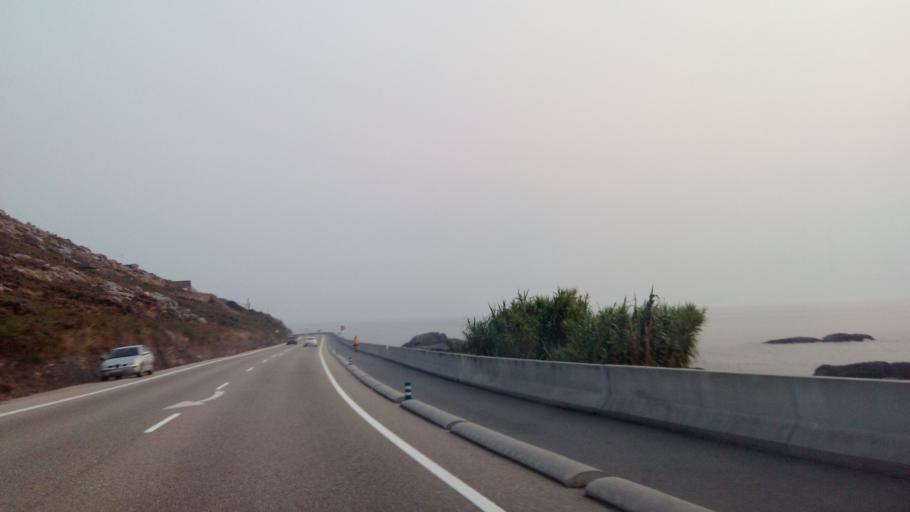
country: ES
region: Galicia
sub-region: Provincia de Pontevedra
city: Baiona
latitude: 42.1070
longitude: -8.8971
